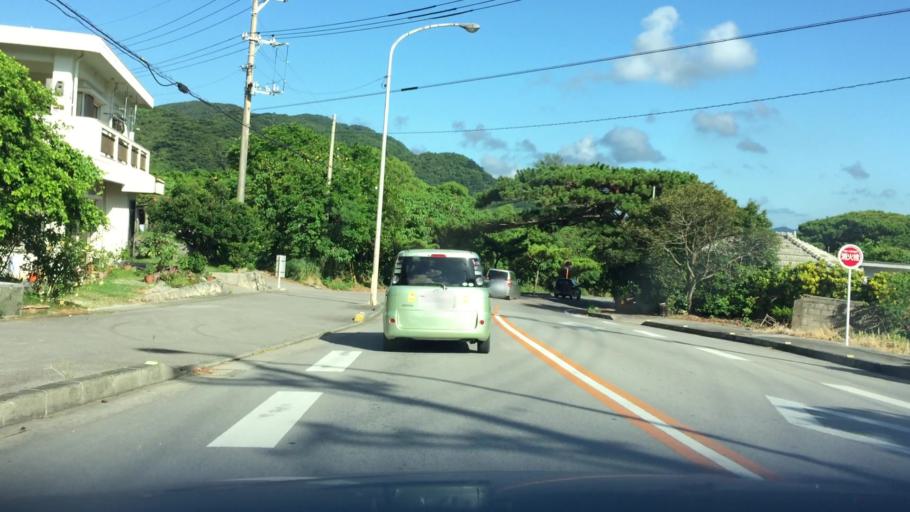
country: JP
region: Okinawa
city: Ishigaki
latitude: 24.4393
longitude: 124.1185
